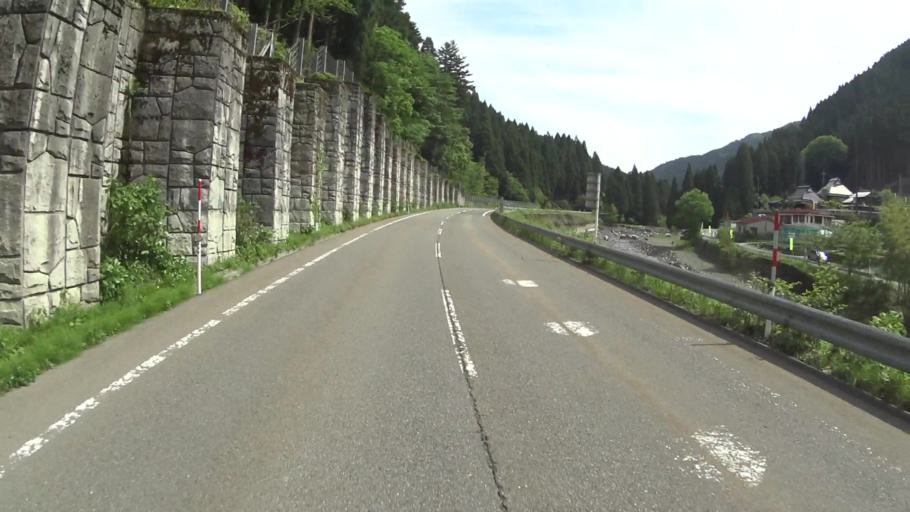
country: JP
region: Shiga Prefecture
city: Kitahama
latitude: 35.2337
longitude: 135.8633
